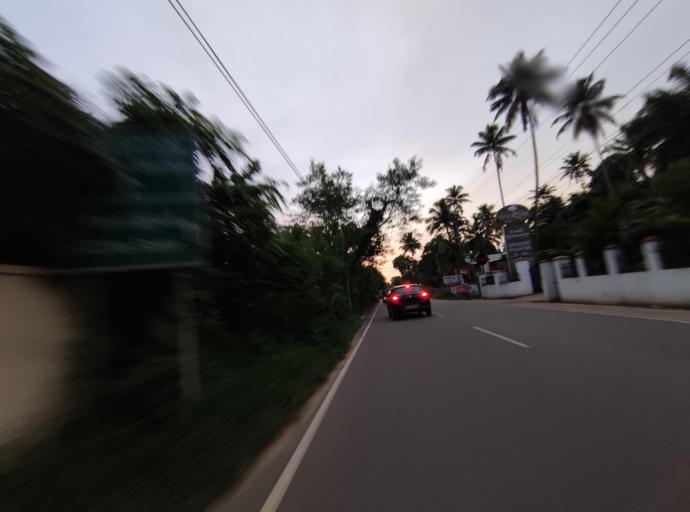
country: IN
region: Kerala
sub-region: Alappuzha
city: Shertallai
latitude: 9.6853
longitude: 76.3482
